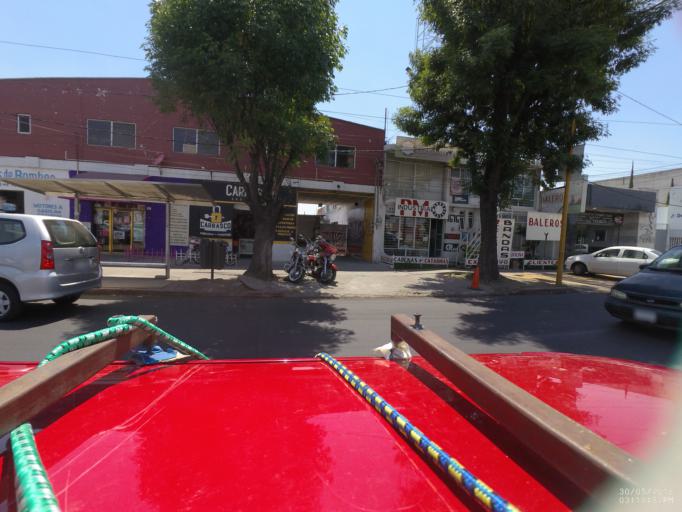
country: MX
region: Aguascalientes
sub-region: Aguascalientes
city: Aguascalientes
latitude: 21.8900
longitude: -102.3126
